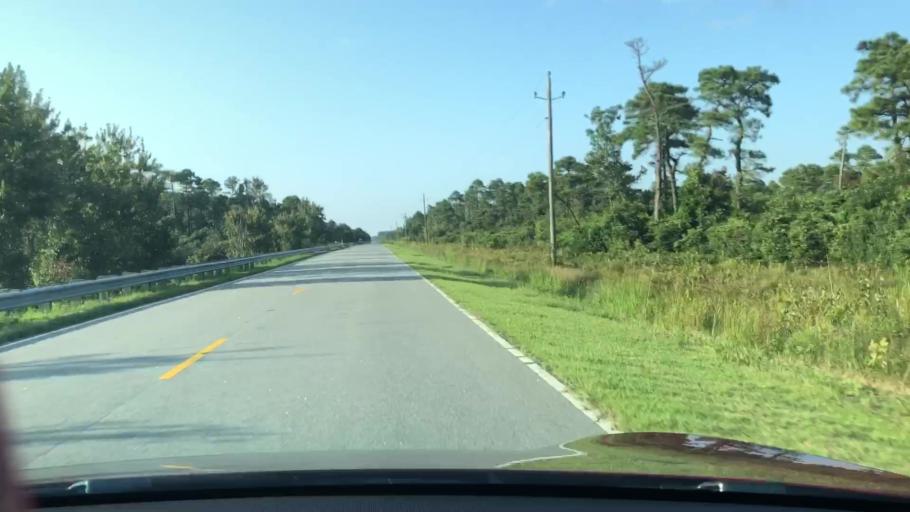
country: US
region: North Carolina
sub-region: Dare County
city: Wanchese
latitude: 35.7445
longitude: -75.7687
